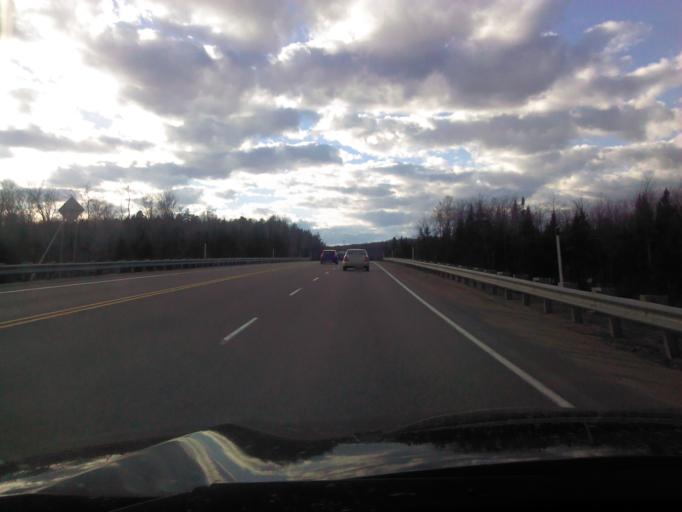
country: CA
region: Quebec
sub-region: Capitale-Nationale
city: Saint-Augustin-de-Desmaures
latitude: 46.7791
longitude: -71.5135
